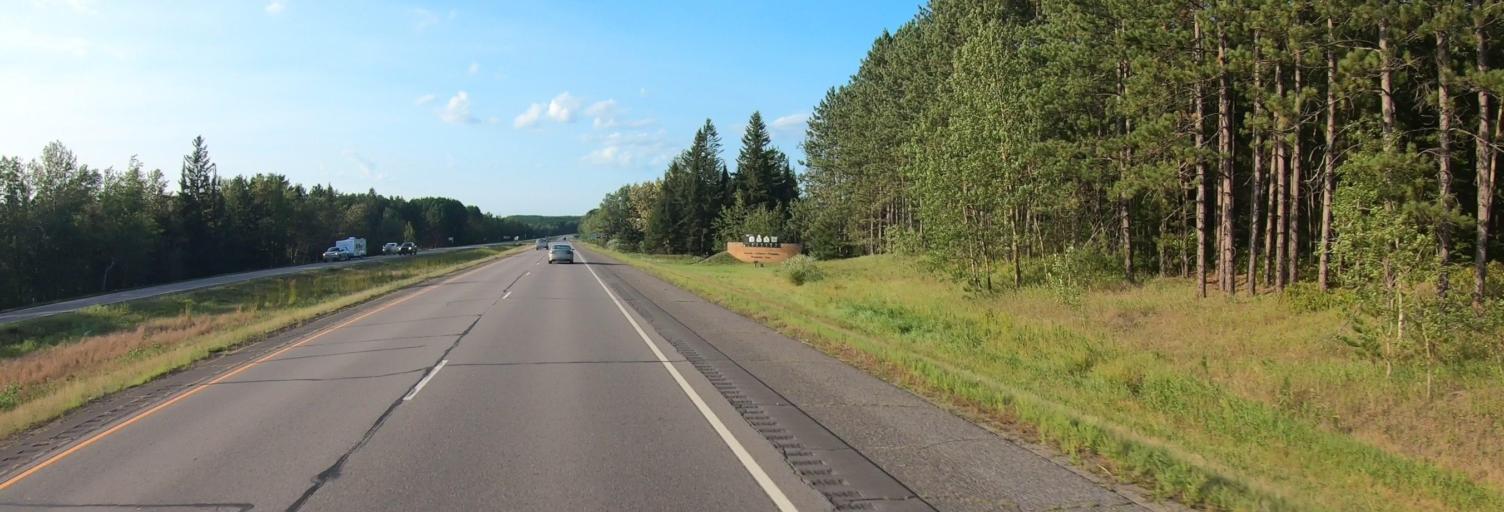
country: US
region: Minnesota
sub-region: Saint Louis County
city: Eveleth
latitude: 47.4261
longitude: -92.5219
